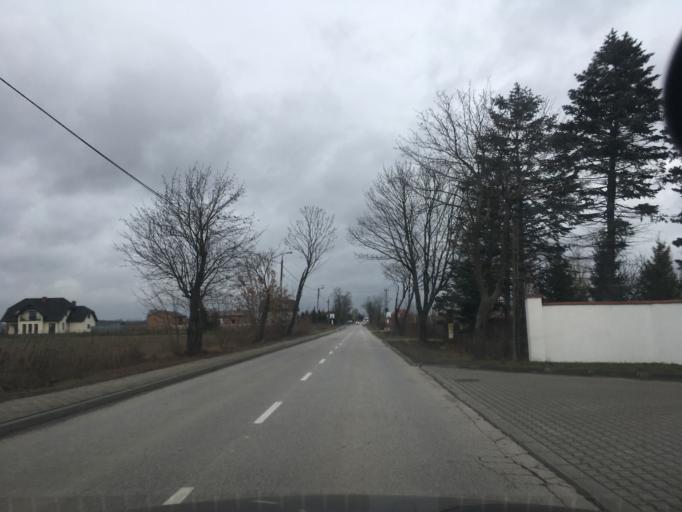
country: PL
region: Masovian Voivodeship
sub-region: Powiat piaseczynski
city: Lesznowola
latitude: 52.1148
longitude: 20.9309
